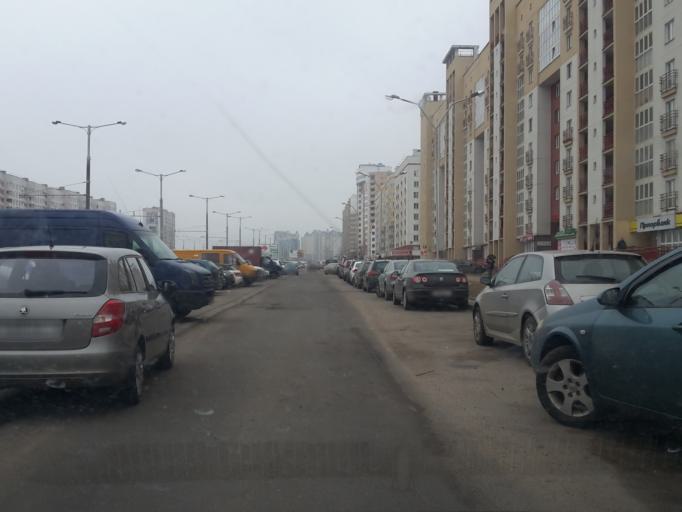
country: BY
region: Minsk
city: Novoye Medvezhino
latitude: 53.9063
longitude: 27.4421
